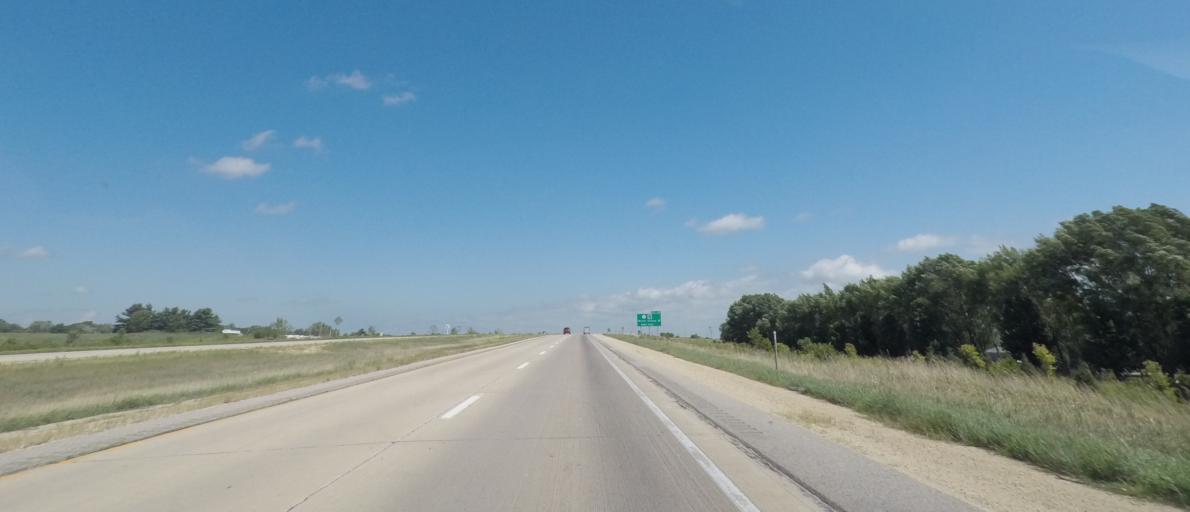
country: US
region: Iowa
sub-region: Jones County
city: Anamosa
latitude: 42.0708
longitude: -91.3405
